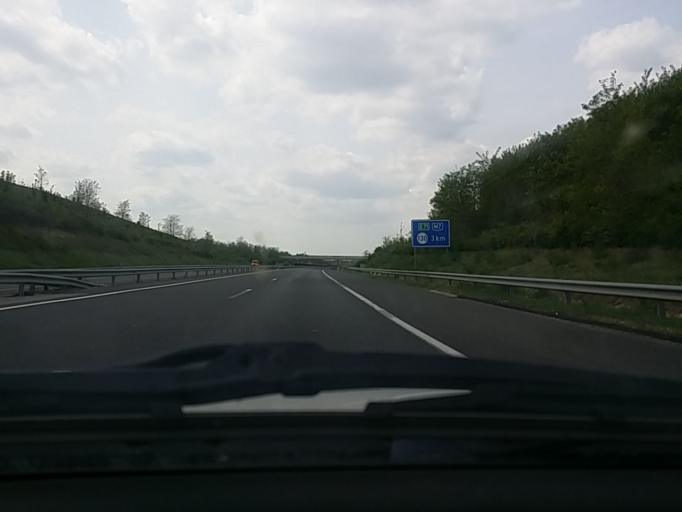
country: HU
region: Somogy
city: Balatonszarszo
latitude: 46.8157
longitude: 17.8508
